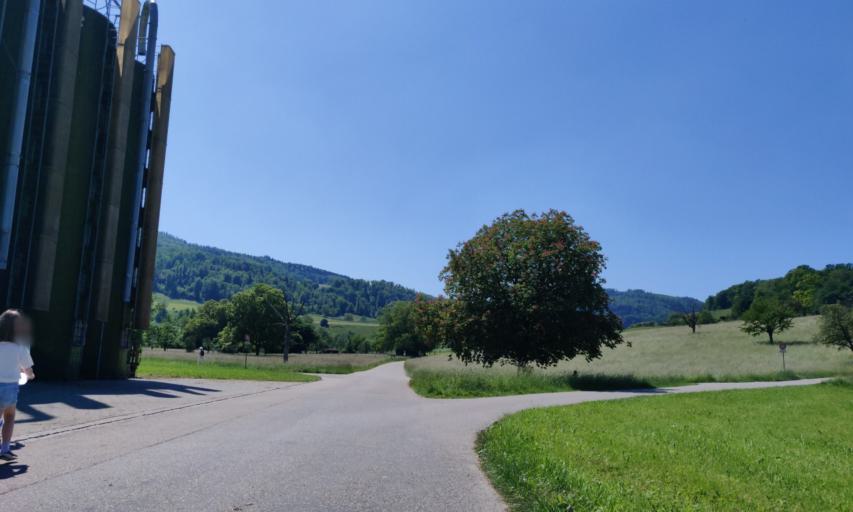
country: CH
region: Basel-Landschaft
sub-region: Bezirk Arlesheim
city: Pfeffingen
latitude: 47.4675
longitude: 7.5884
